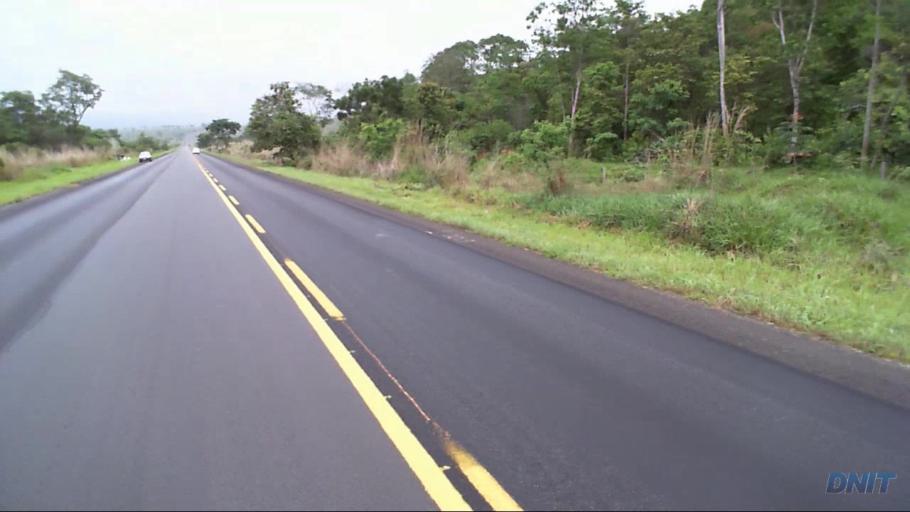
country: BR
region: Goias
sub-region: Padre Bernardo
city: Padre Bernardo
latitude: -15.2037
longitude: -48.4594
